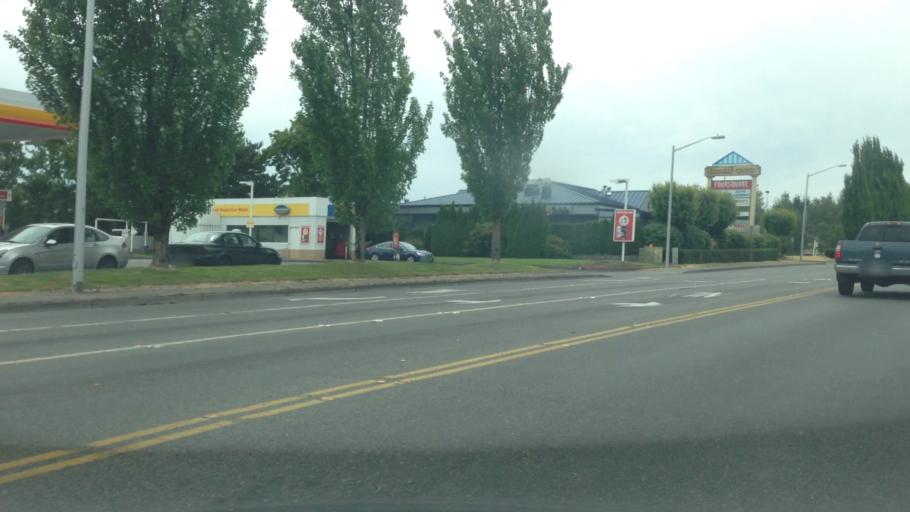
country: US
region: Washington
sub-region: Pierce County
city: South Hill
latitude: 47.1111
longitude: -122.2937
